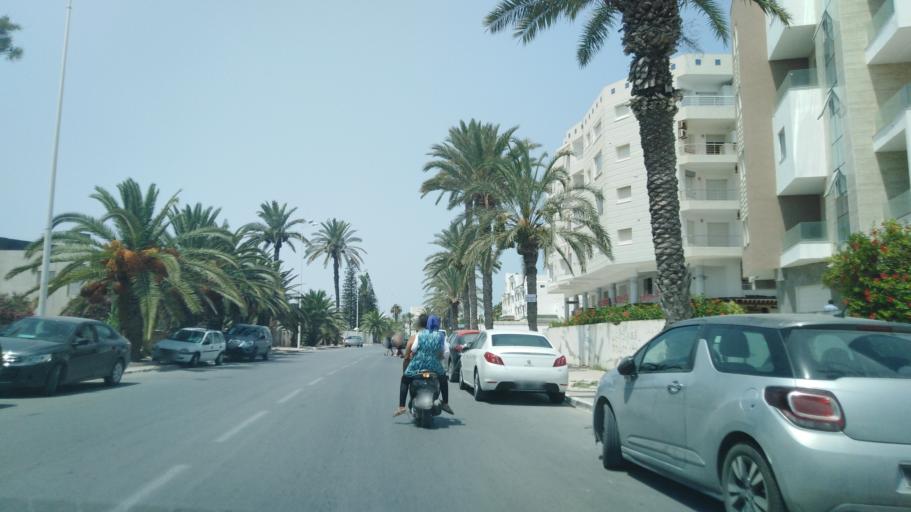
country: TN
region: Al Mahdiyah
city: Mahdia
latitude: 35.5134
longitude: 11.0478
